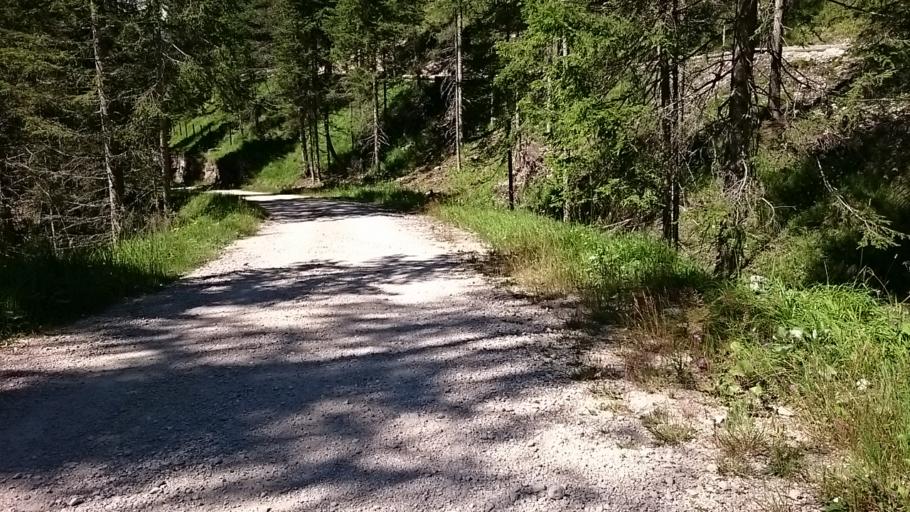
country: IT
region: Veneto
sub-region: Provincia di Belluno
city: Cortina d'Ampezzo
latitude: 46.5997
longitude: 12.1229
